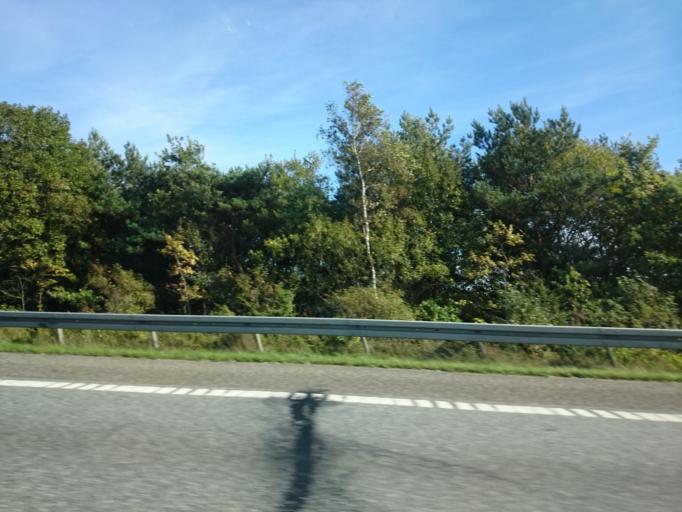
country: DK
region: Central Jutland
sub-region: Skanderborg Kommune
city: Skanderborg
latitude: 56.0178
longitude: 9.8832
